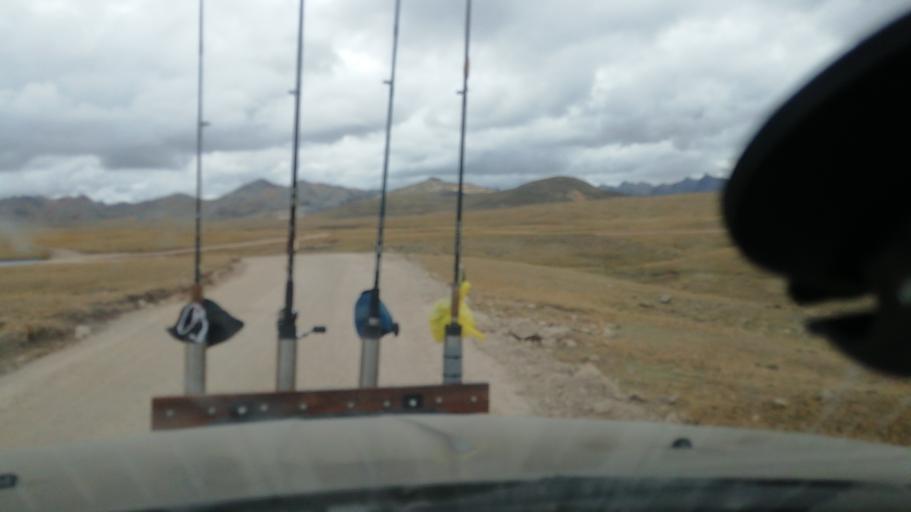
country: PE
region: Huancavelica
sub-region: Provincia de Huancavelica
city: Acobambilla
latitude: -12.5424
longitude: -75.5482
